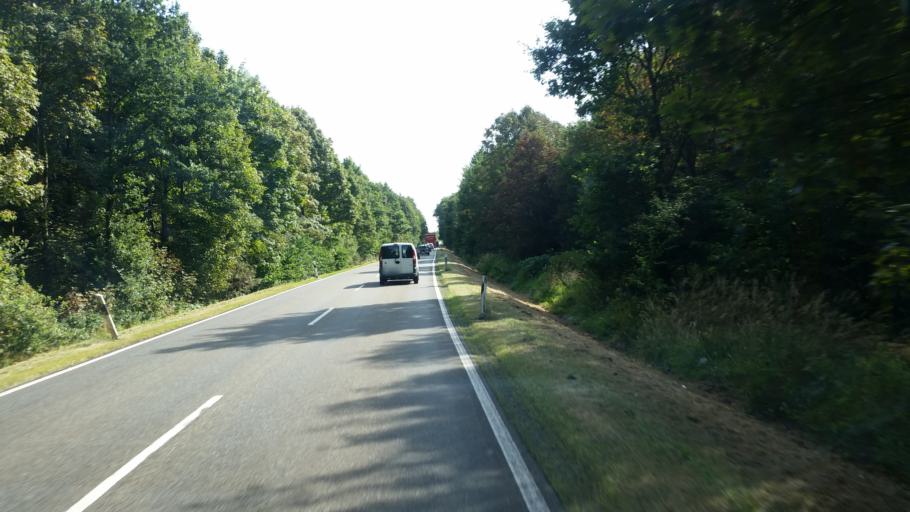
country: DE
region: Rheinland-Pfalz
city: Hartlingen
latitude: 50.5409
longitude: 7.8855
